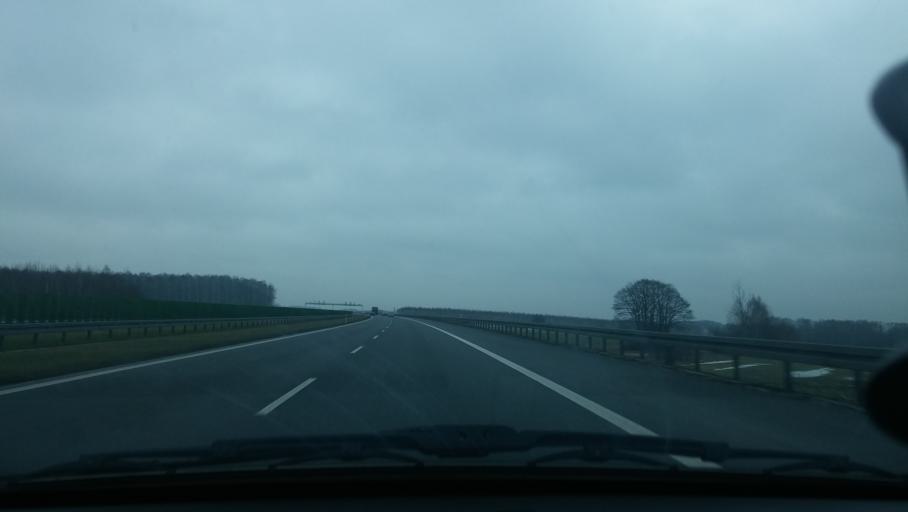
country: PL
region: Masovian Voivodeship
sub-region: Powiat minski
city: Minsk Mazowiecki
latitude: 52.2094
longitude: 21.5824
